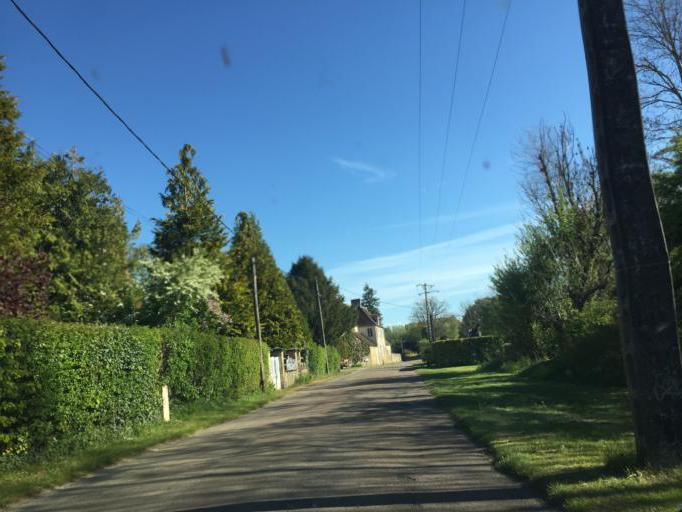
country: FR
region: Bourgogne
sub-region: Departement de la Nievre
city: Clamecy
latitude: 47.5070
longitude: 3.5161
